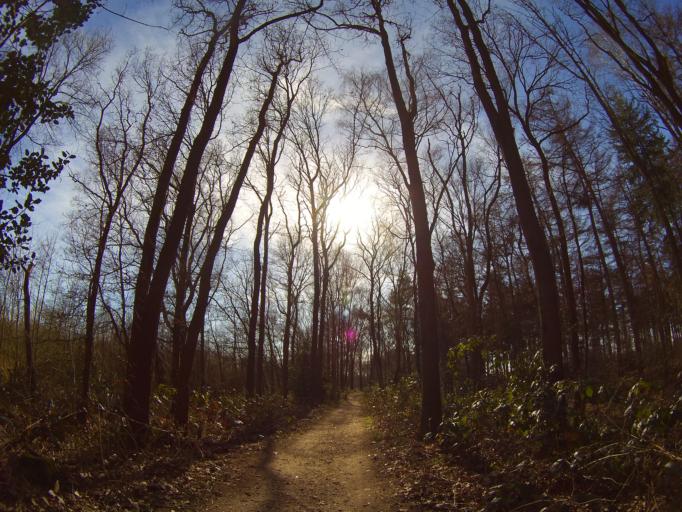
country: NL
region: Utrecht
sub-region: Gemeente Utrechtse Heuvelrug
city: Overberg
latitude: 52.0793
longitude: 5.5253
